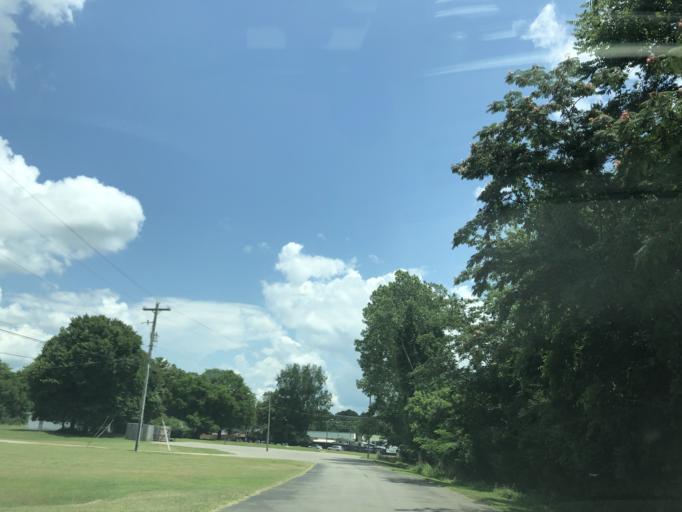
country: US
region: Tennessee
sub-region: Davidson County
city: Lakewood
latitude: 36.2020
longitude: -86.6241
